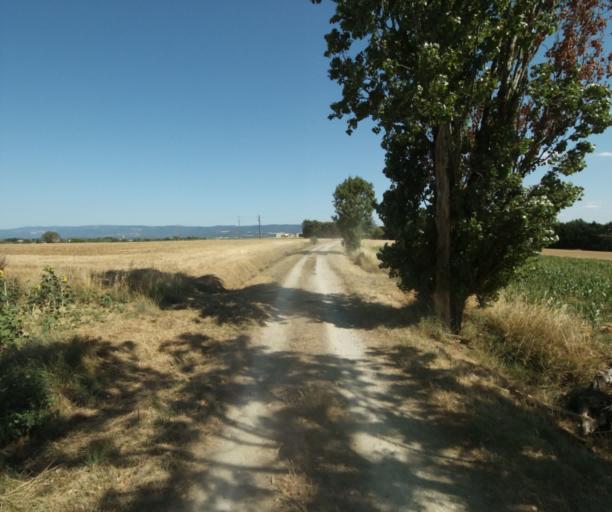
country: FR
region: Midi-Pyrenees
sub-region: Departement de la Haute-Garonne
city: Saint-Felix-Lauragais
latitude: 43.4816
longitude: 1.9068
